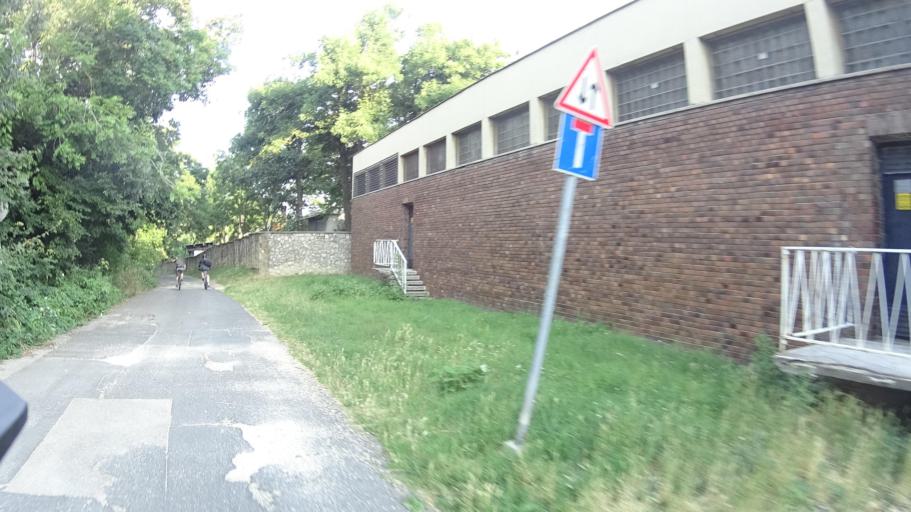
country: HU
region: Pest
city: Budaors
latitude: 47.4870
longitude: 18.9532
